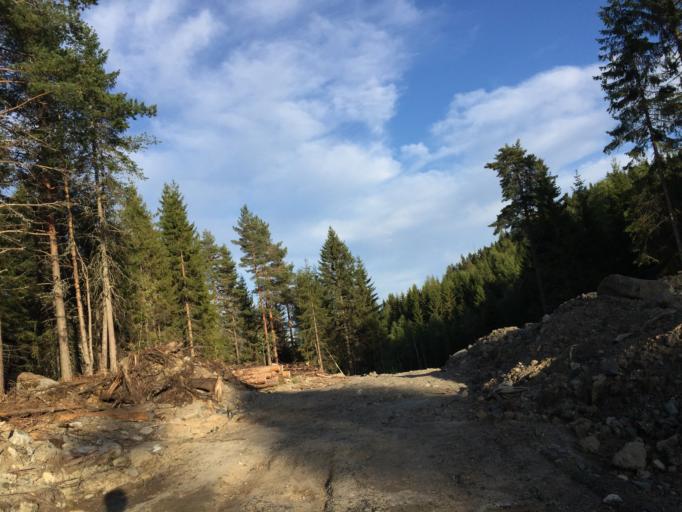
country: NO
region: Akershus
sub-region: Raelingen
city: Fjerdingby
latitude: 59.9289
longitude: 11.0446
